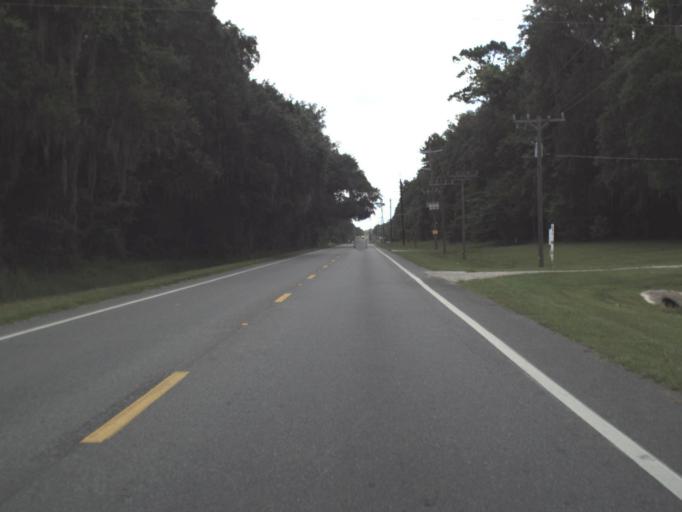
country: US
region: Florida
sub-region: Putnam County
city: East Palatka
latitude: 29.5932
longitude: -81.6013
